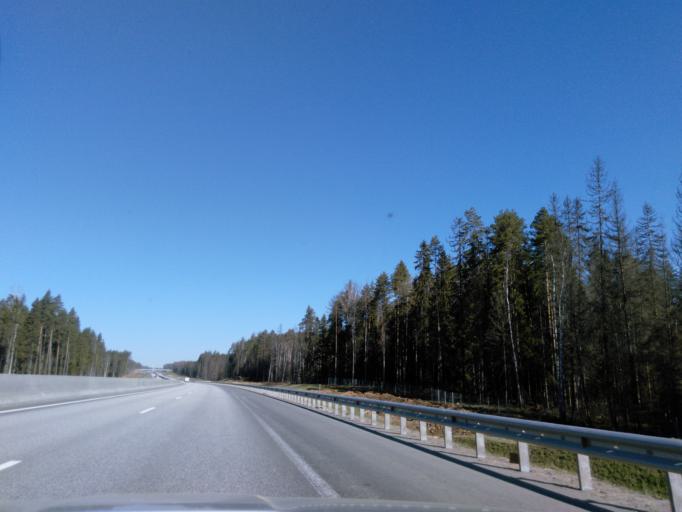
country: RU
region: Moskovskaya
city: Mendeleyevo
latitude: 56.0529
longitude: 37.2566
